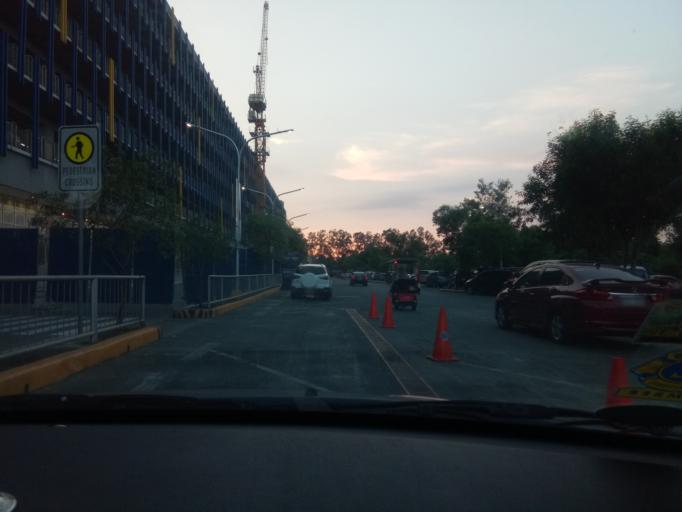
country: PH
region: Calabarzon
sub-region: Province of Cavite
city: Dasmarinas
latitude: 14.3016
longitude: 120.9577
